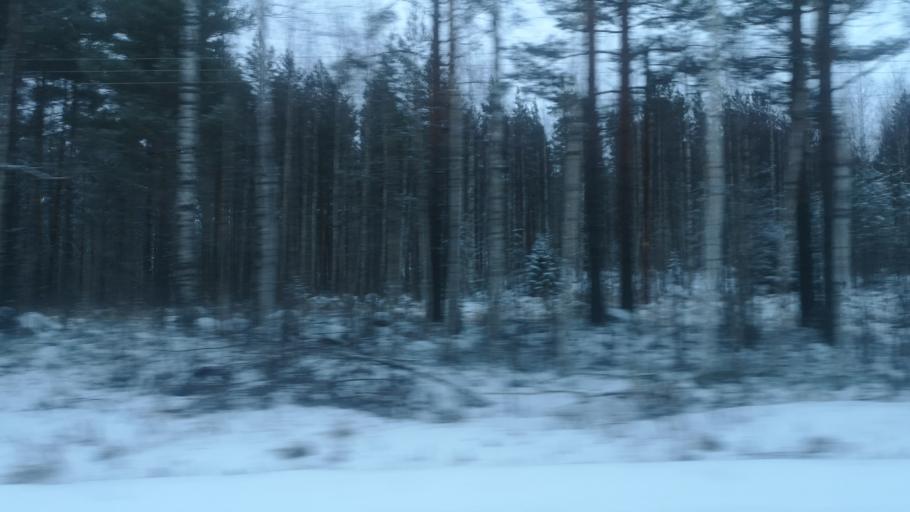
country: FI
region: Southern Savonia
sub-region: Savonlinna
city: Enonkoski
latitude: 62.0953
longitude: 28.6684
